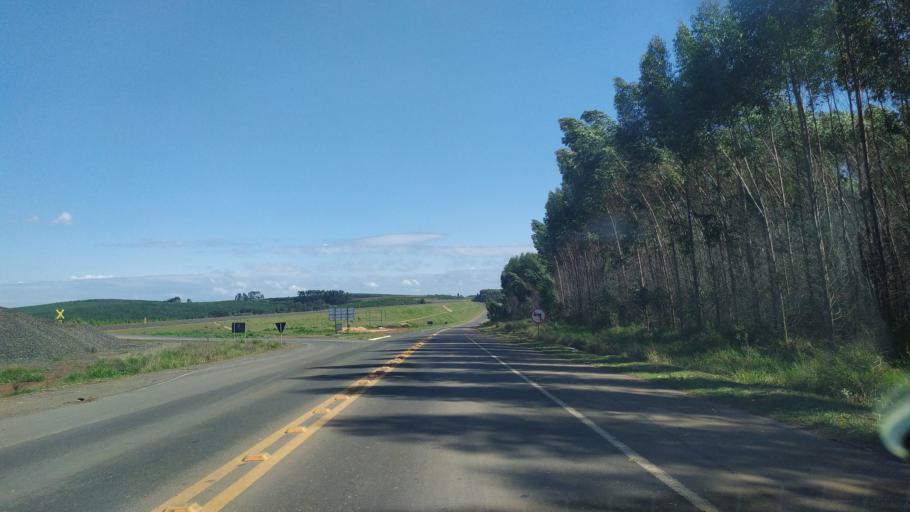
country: BR
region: Parana
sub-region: Telemaco Borba
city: Telemaco Borba
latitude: -24.2402
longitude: -50.7653
